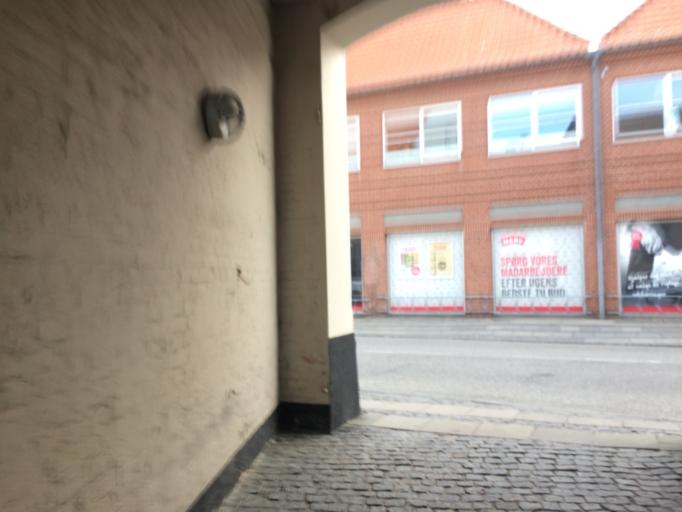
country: DK
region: Capital Region
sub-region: Bornholm Kommune
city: Ronne
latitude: 55.1014
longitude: 14.7006
